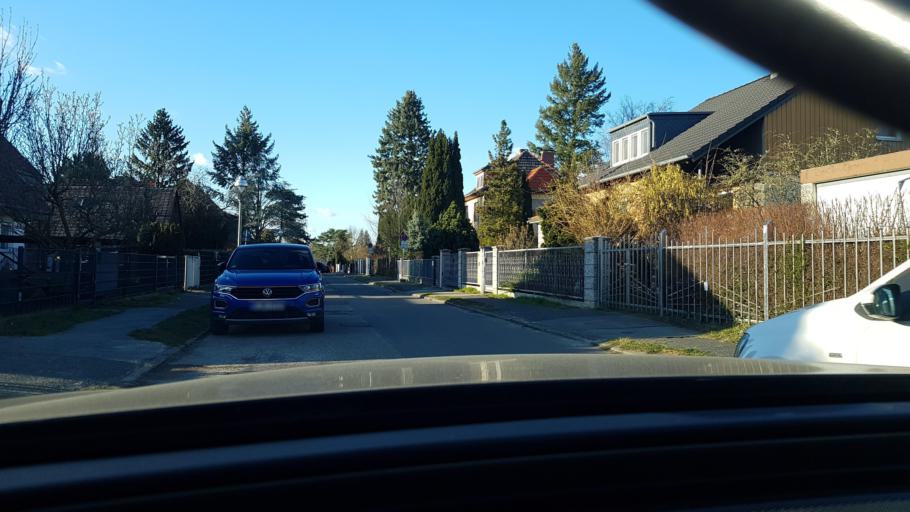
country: DE
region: Berlin
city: Rudow
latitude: 52.4144
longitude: 13.5045
